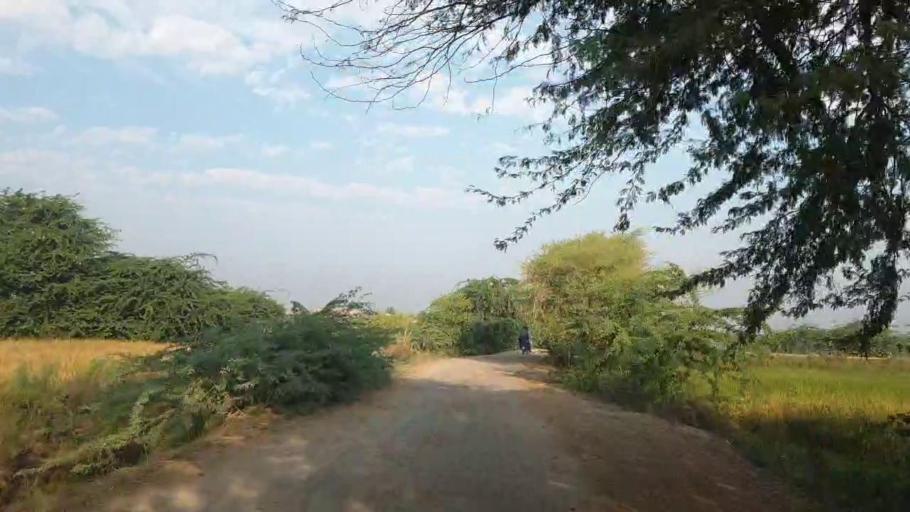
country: PK
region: Sindh
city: Tando Bago
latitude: 24.8100
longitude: 68.9570
